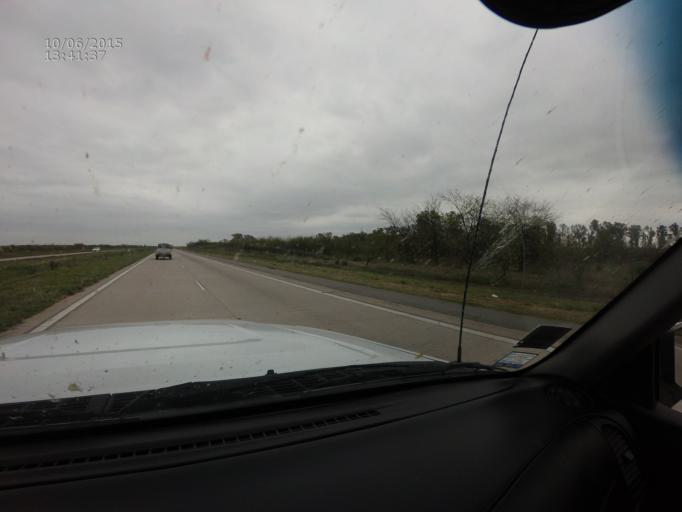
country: AR
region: Cordoba
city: Bell Ville
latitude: -32.5919
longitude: -62.5034
